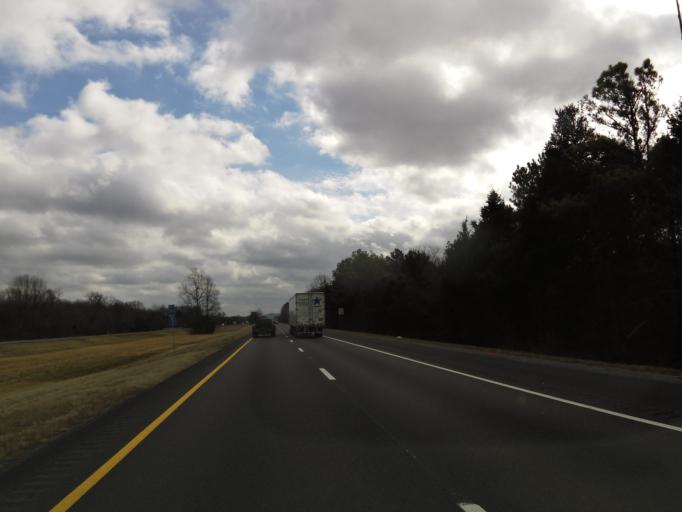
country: US
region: Tennessee
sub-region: Rutherford County
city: Plainview
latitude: 35.7174
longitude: -86.3173
